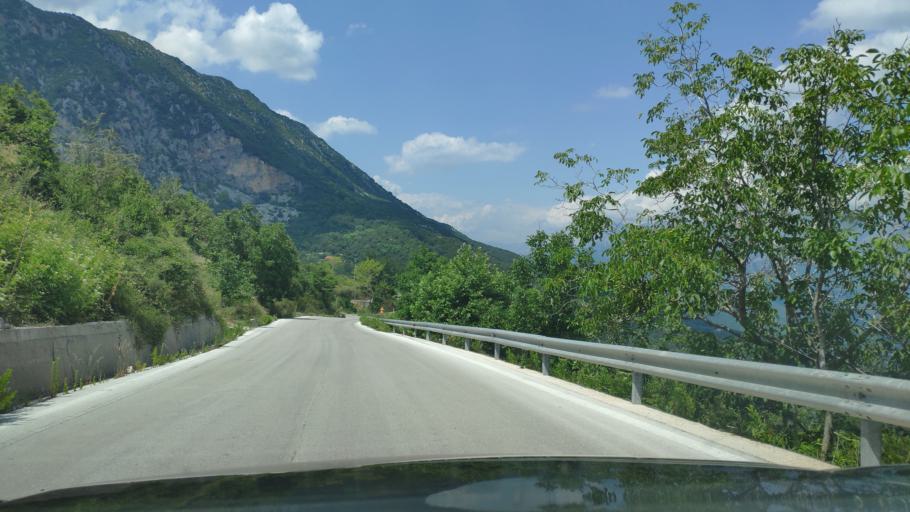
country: GR
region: Epirus
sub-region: Nomos Artas
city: Agios Dimitrios
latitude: 39.3384
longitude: 21.0063
